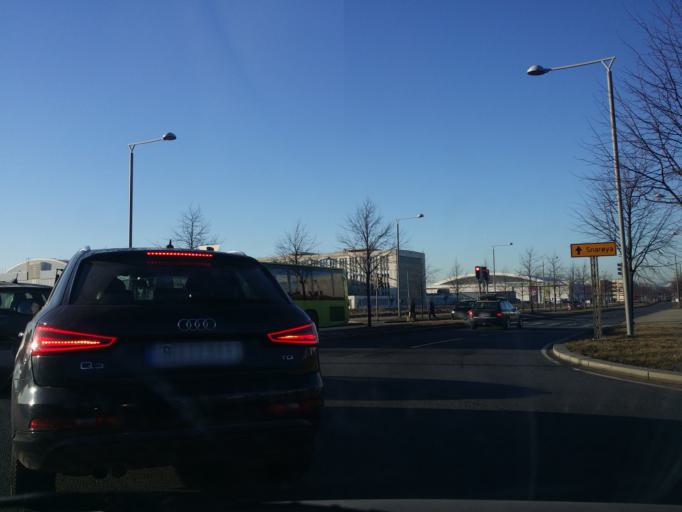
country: NO
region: Akershus
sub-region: Baerum
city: Lysaker
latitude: 59.8951
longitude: 10.6255
